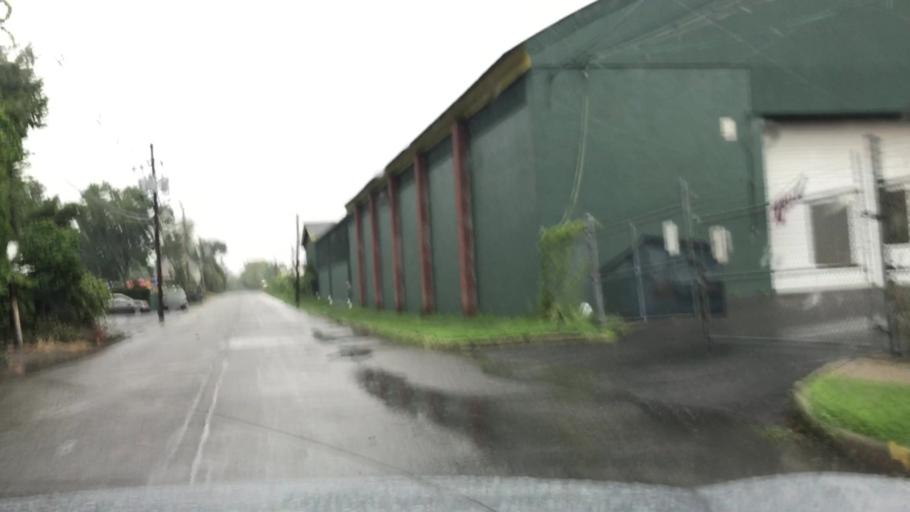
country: US
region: New Jersey
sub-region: Bergen County
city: Closter
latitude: 40.9750
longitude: -73.9614
